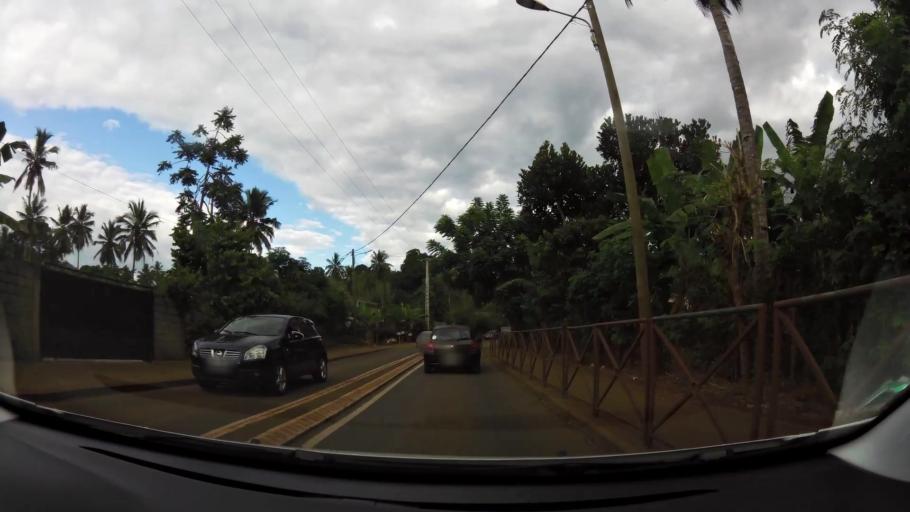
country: YT
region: Dembeni
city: Dembeni
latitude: -12.8386
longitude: 45.1720
